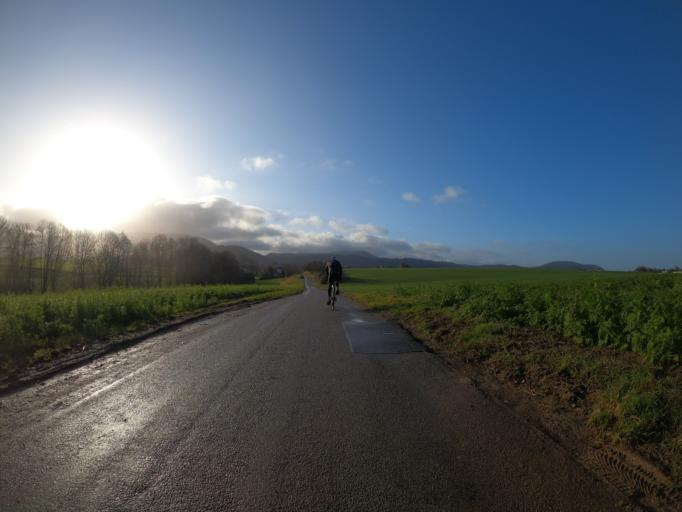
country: DE
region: Baden-Wuerttemberg
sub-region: Regierungsbezirk Stuttgart
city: Boll
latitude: 48.6498
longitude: 9.6213
